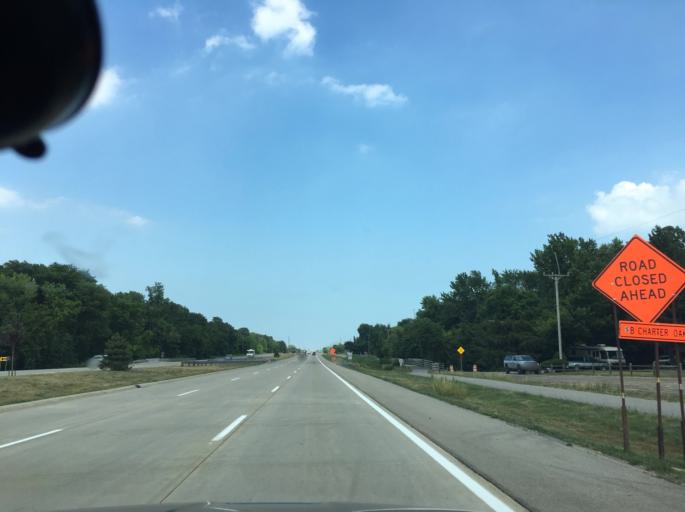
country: US
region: Michigan
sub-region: Macomb County
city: Clinton
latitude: 42.5686
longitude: -82.9303
